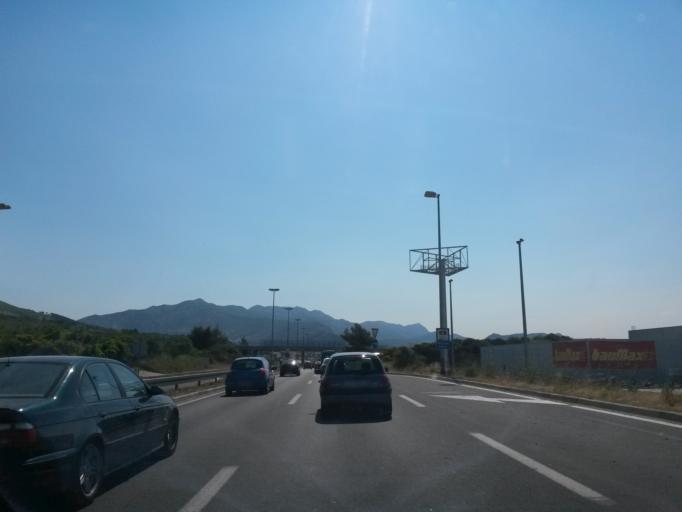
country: HR
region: Splitsko-Dalmatinska
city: Vranjic
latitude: 43.5452
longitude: 16.4522
